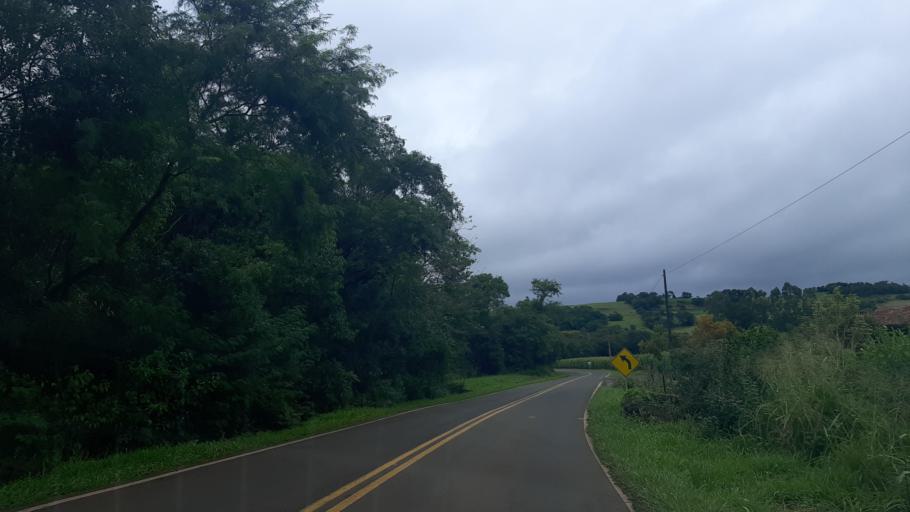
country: BR
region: Parana
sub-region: Ampere
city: Ampere
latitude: -25.9981
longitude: -53.4391
